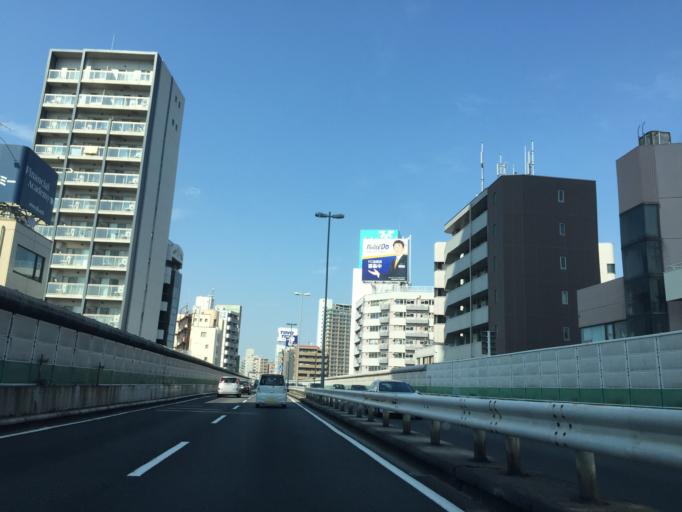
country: JP
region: Tokyo
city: Tokyo
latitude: 35.6326
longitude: 139.6600
